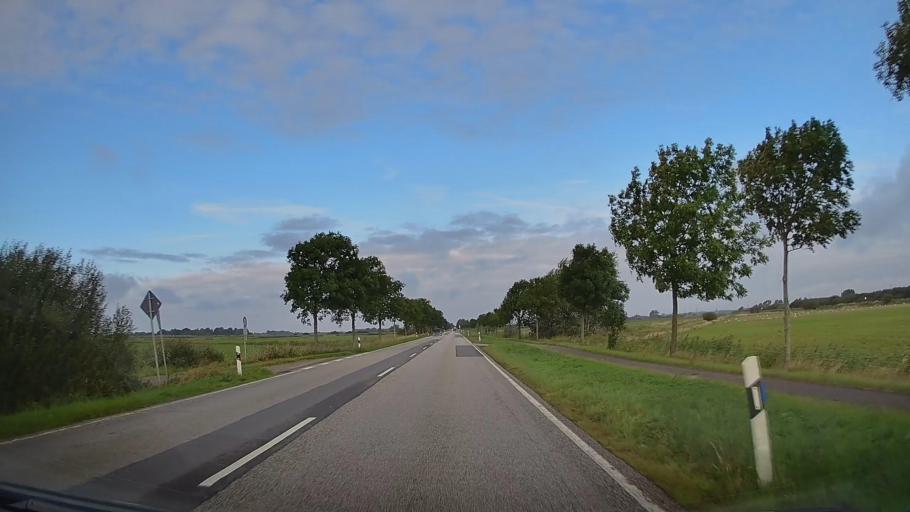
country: DE
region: Schleswig-Holstein
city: Wobbenbull
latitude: 54.5382
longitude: 9.0154
